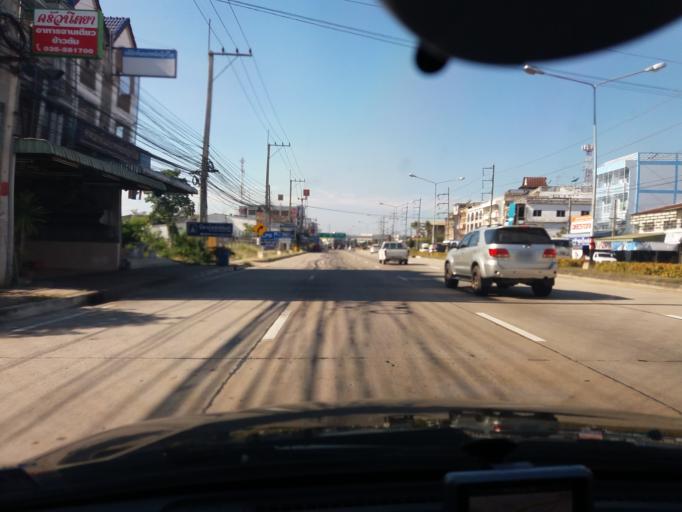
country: TH
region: Suphan Buri
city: Si Prachan
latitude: 14.6186
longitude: 100.1491
